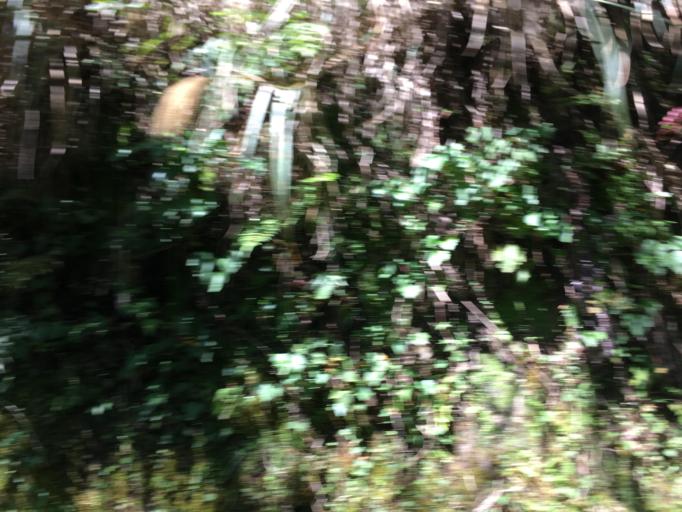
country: TW
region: Taiwan
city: Daxi
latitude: 24.5471
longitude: 121.4012
